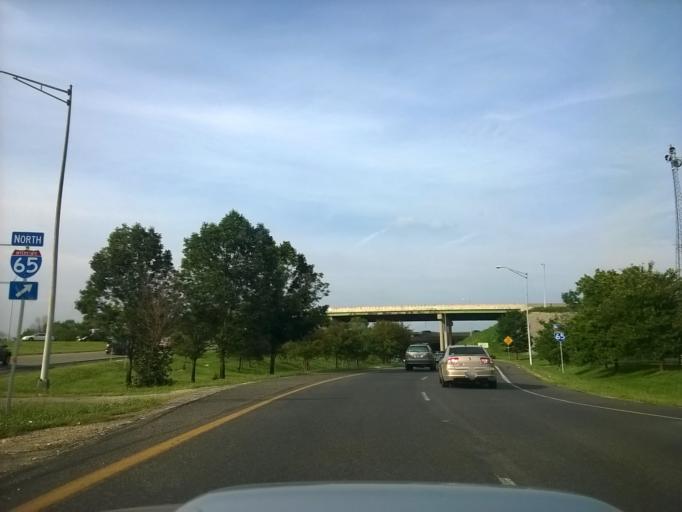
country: US
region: Indiana
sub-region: Marion County
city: Indianapolis
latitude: 39.7825
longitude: -86.1673
